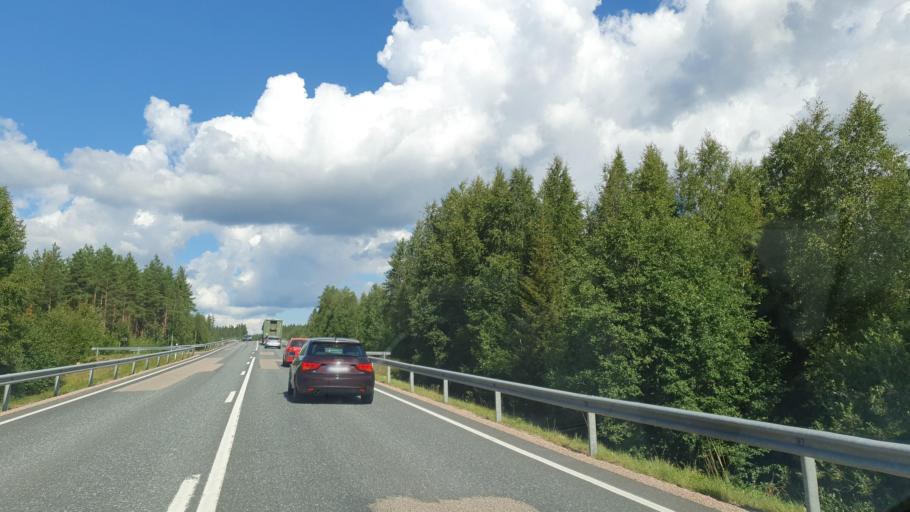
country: FI
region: Kainuu
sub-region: Kajaani
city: Kajaani
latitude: 64.0807
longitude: 27.4528
